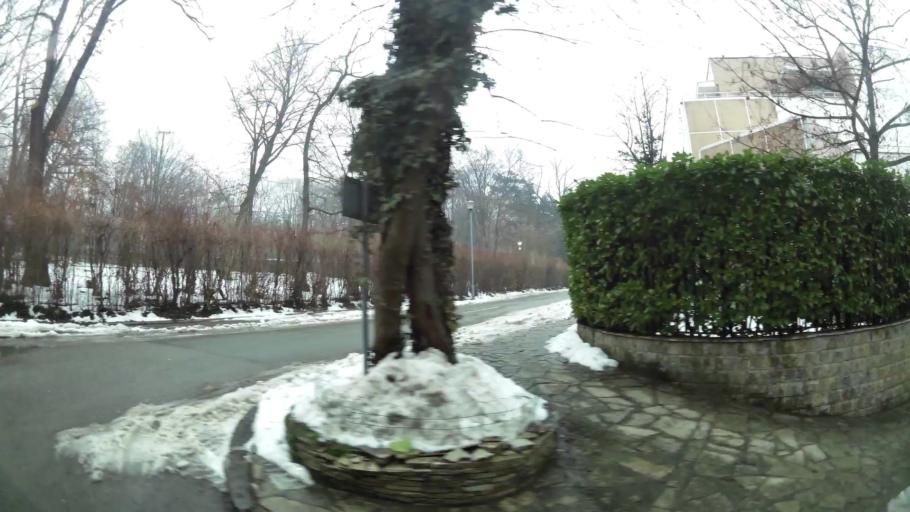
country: RS
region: Central Serbia
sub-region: Belgrade
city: Savski Venac
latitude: 44.7859
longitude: 20.4446
